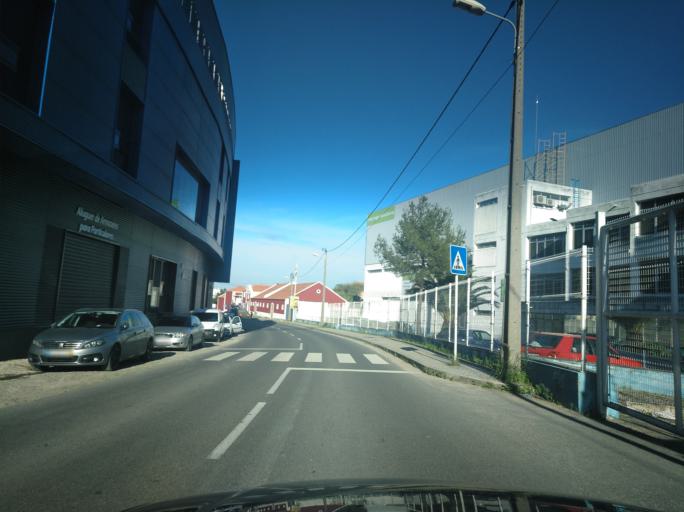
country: PT
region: Lisbon
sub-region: Loures
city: Sacavem
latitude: 38.7865
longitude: -9.1167
